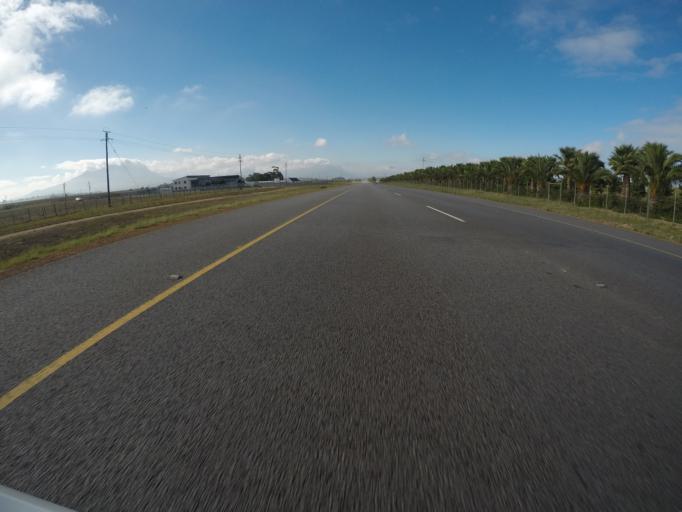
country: ZA
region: Western Cape
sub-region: City of Cape Town
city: Kraaifontein
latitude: -33.8386
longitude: 18.7990
